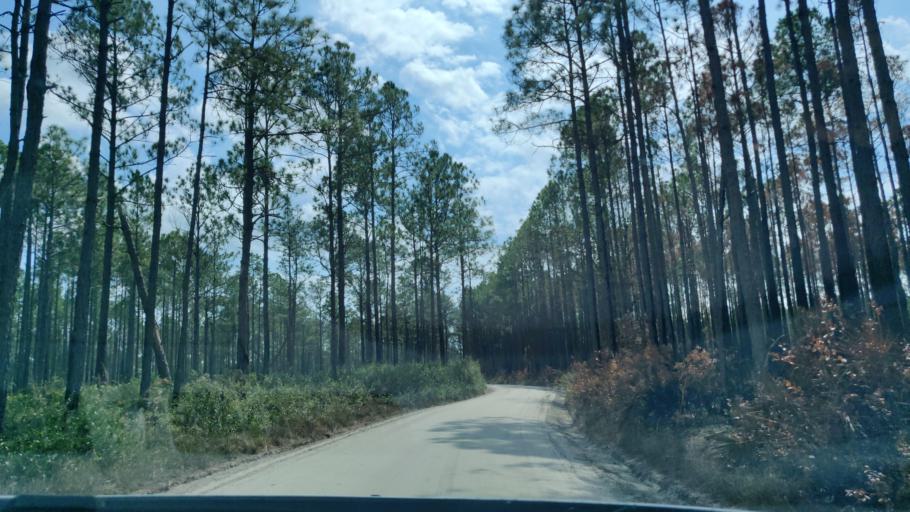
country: US
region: Florida
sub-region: Clay County
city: Middleburg
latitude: 30.1658
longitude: -81.9491
